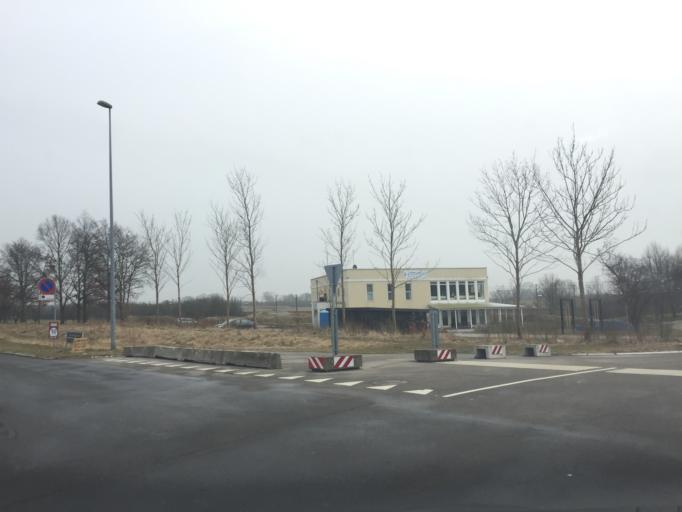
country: DK
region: Capital Region
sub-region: Hoje-Taastrup Kommune
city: Flong
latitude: 55.6482
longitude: 12.2090
